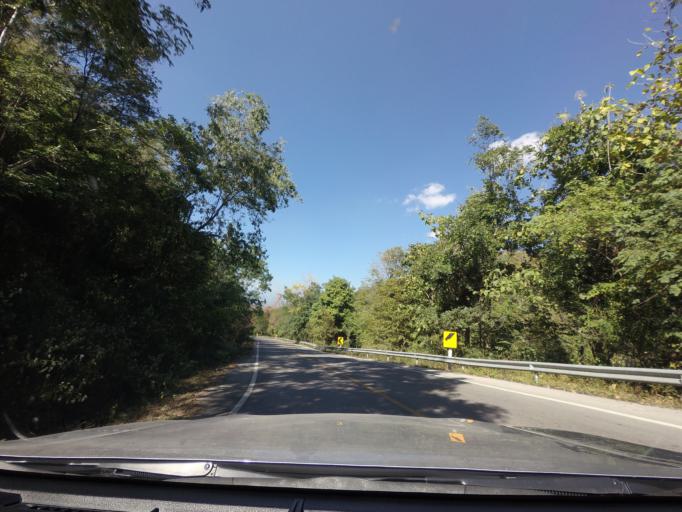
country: TH
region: Lampang
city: Chae Hom
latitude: 18.6336
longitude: 99.6115
